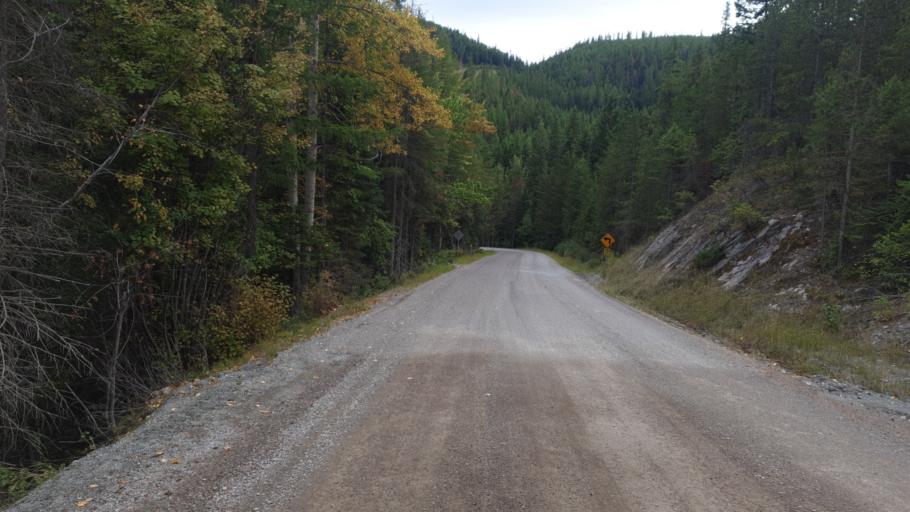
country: US
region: Montana
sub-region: Flathead County
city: Lakeside
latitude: 47.9876
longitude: -114.3150
